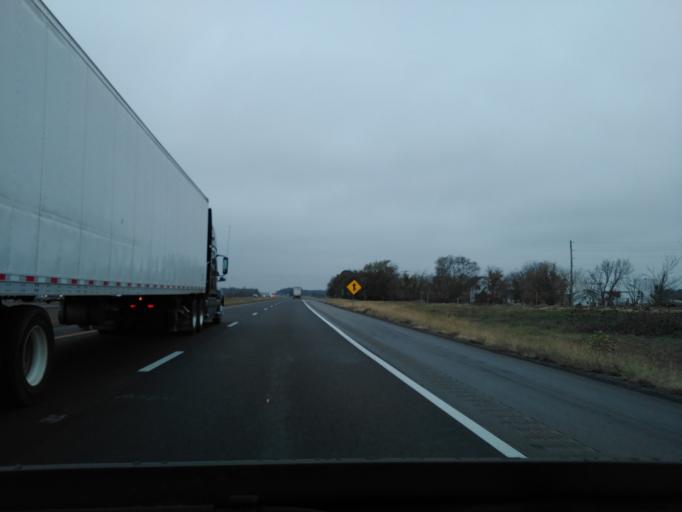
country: US
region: Illinois
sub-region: Madison County
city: Highland
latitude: 38.7862
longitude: -89.6332
